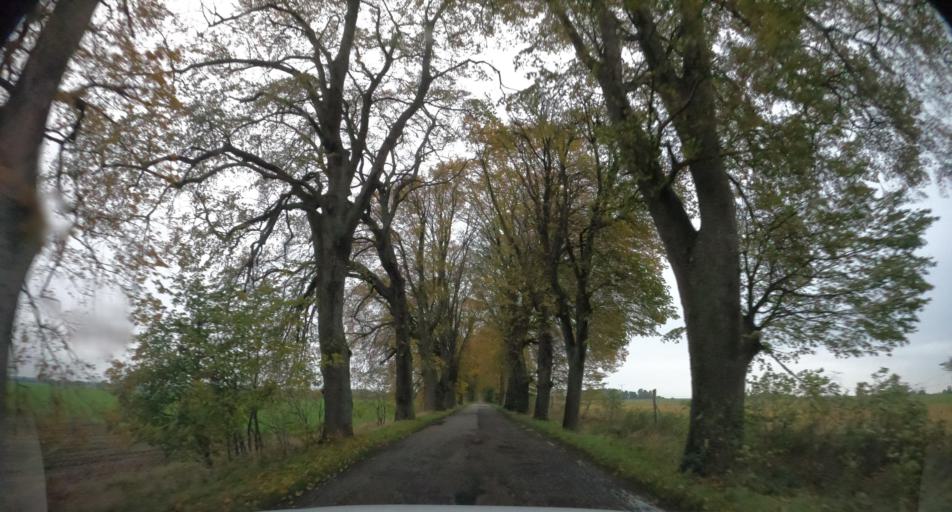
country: PL
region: West Pomeranian Voivodeship
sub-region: Powiat kamienski
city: Wolin
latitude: 53.9006
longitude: 14.6281
